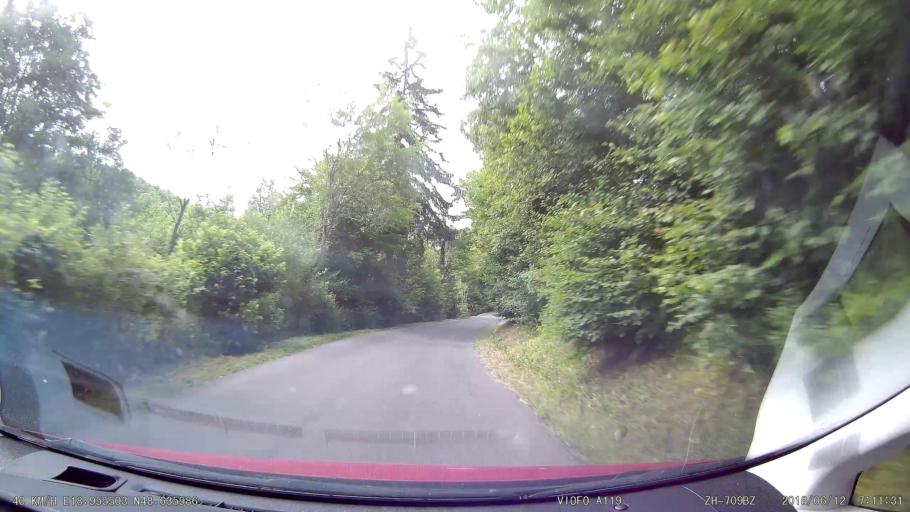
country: SK
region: Banskobystricky
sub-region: Okres Ziar nad Hronom
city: Kremnica
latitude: 48.6361
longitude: 18.9554
